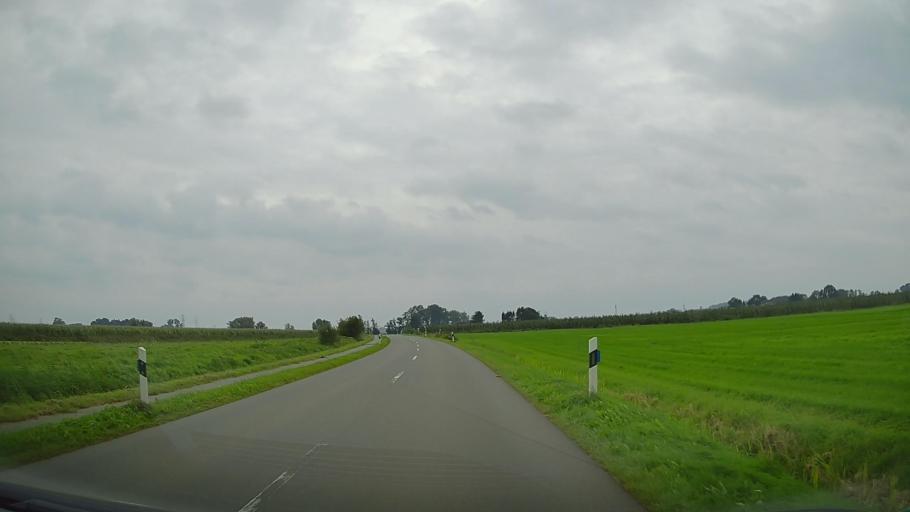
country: DE
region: Lower Saxony
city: Stade
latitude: 53.6324
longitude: 9.4642
